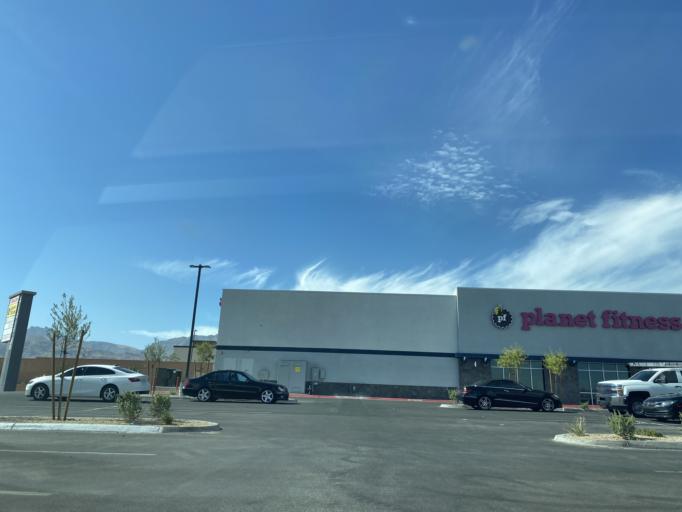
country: US
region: Nevada
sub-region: Clark County
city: Summerlin South
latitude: 36.2834
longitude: -115.3119
